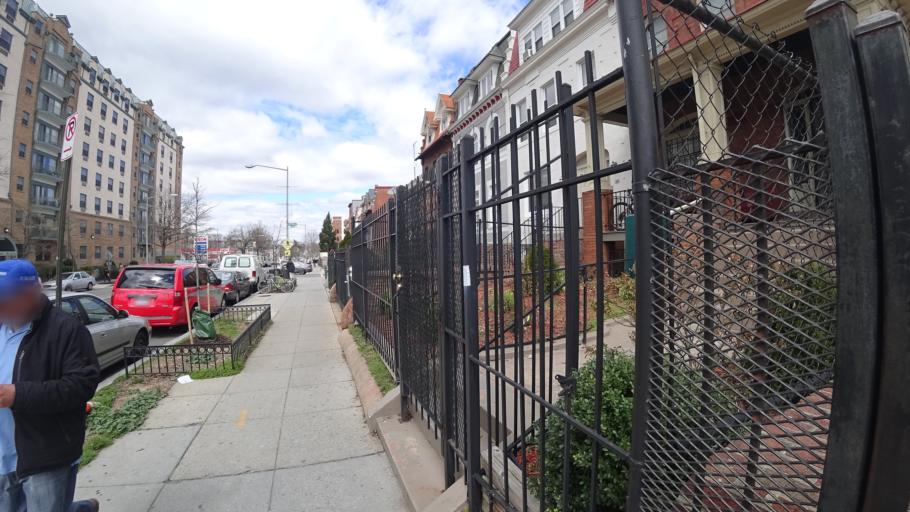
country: US
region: Washington, D.C.
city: Washington, D.C.
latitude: 38.9342
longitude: -77.0326
